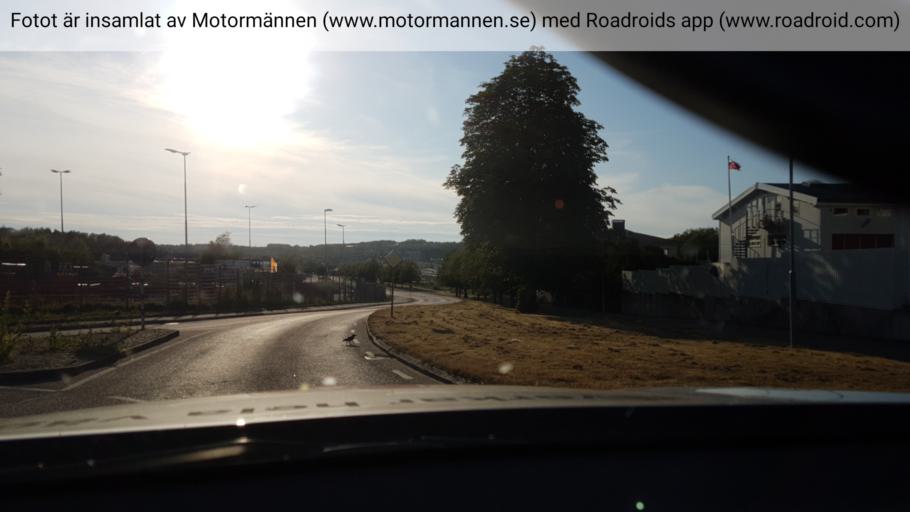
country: SE
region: Vaestra Goetaland
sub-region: Goteborg
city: Majorna
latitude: 57.6586
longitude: 11.9455
